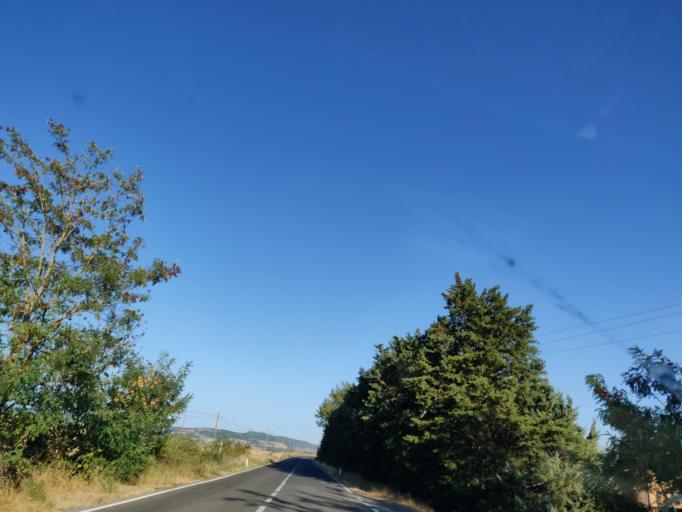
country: IT
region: Tuscany
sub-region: Provincia di Siena
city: Piancastagnaio
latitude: 42.8186
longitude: 11.7353
